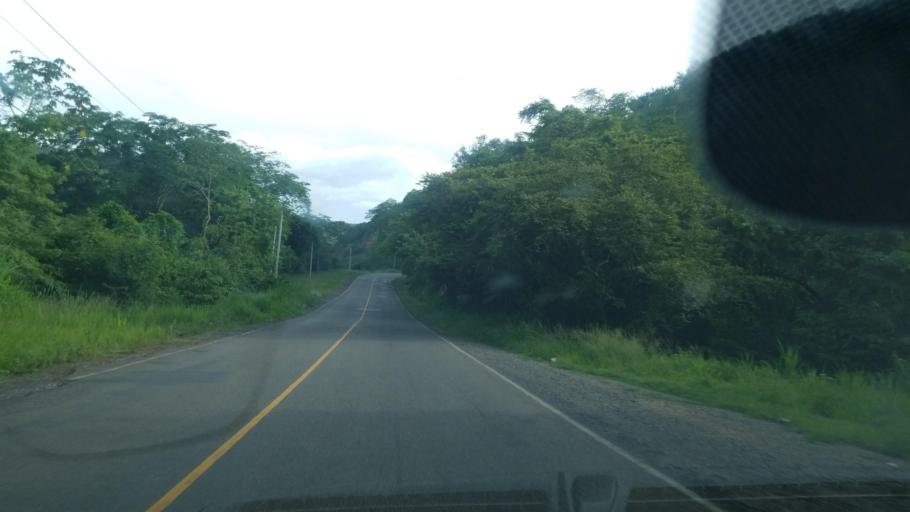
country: HN
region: Santa Barbara
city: Ilama
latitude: 15.0981
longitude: -88.2042
